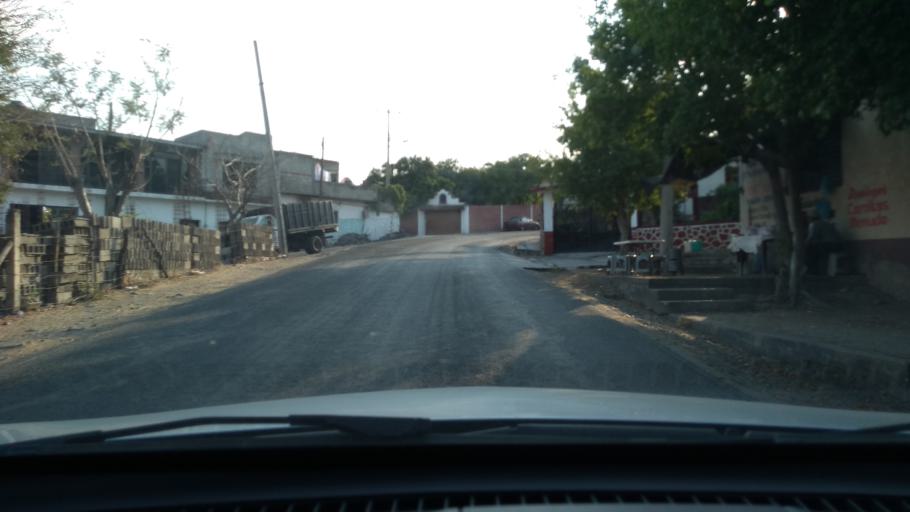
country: MX
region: Morelos
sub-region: Jojutla
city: Tehuixtla
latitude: 18.5627
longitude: -99.2737
